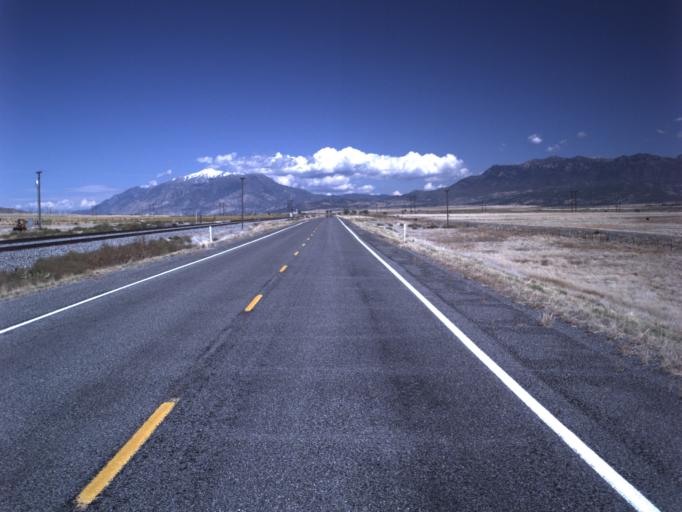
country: US
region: Utah
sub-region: Juab County
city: Nephi
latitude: 39.5185
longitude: -111.9413
